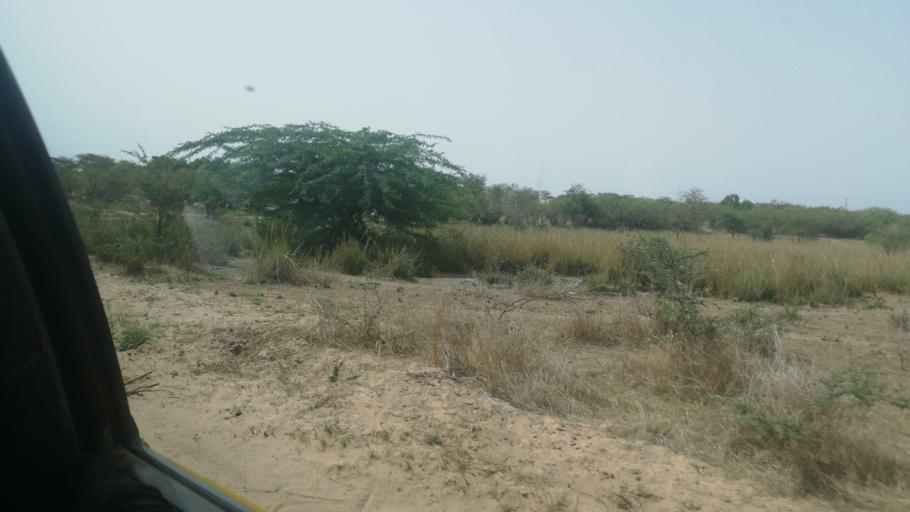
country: SN
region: Saint-Louis
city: Saint-Louis
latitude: 16.0526
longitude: -16.3372
